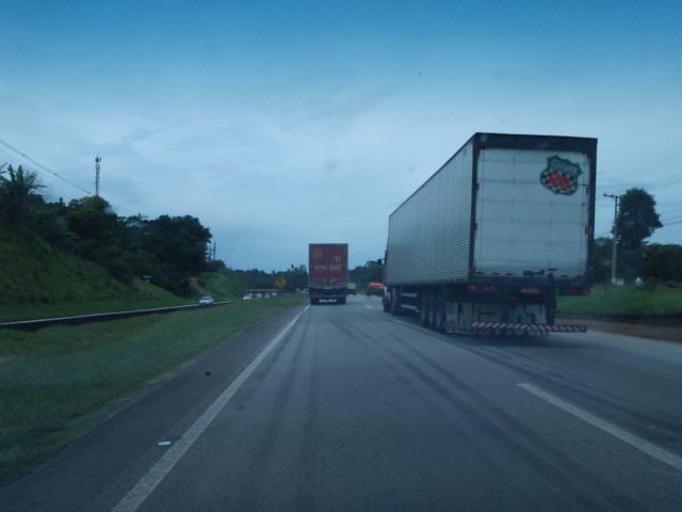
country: BR
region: Sao Paulo
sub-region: Juquitiba
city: Juquitiba
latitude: -23.9350
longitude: -47.0307
